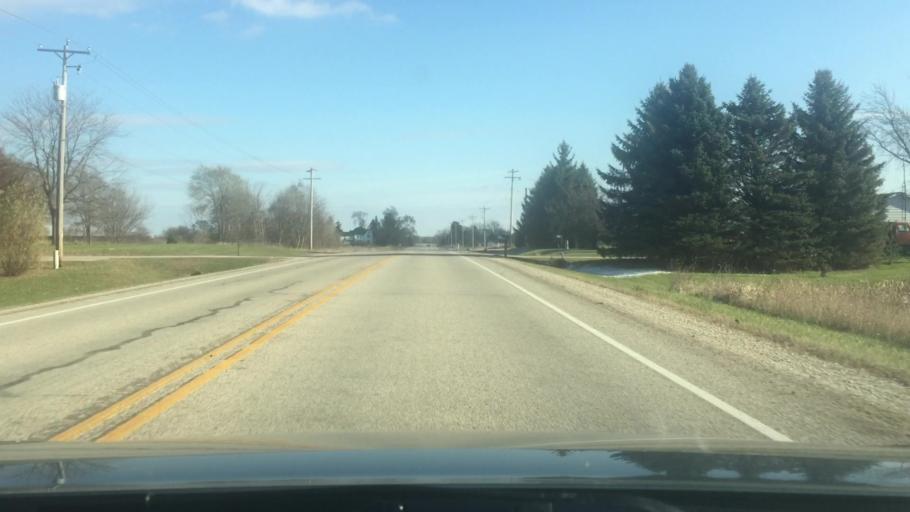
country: US
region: Wisconsin
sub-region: Jefferson County
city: Jefferson
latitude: 42.9370
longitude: -88.7358
